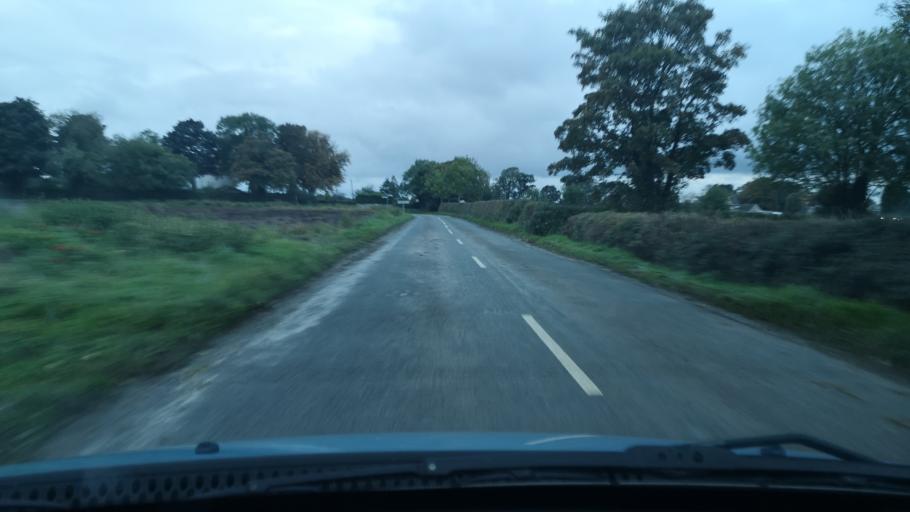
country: GB
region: England
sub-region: Doncaster
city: Norton
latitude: 53.6399
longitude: -1.2167
